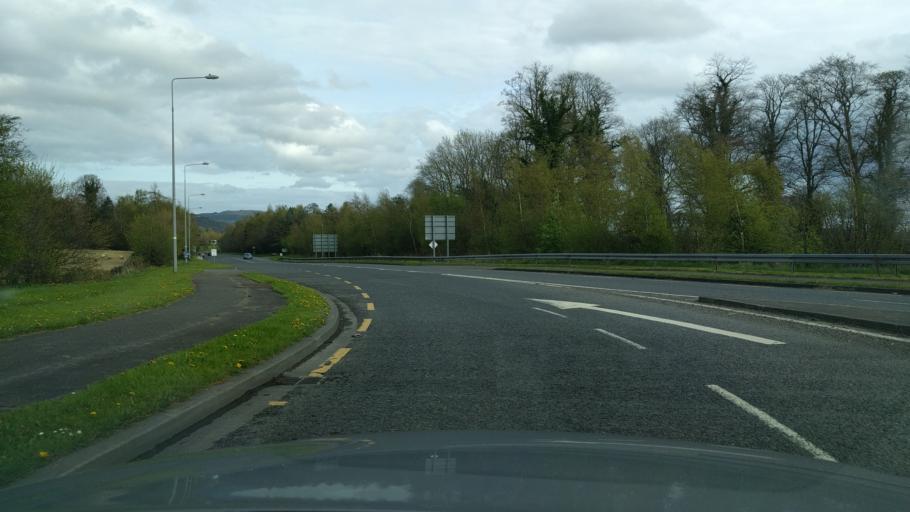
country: IE
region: Leinster
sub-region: Lu
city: Dundalk
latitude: 54.0352
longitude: -6.3841
